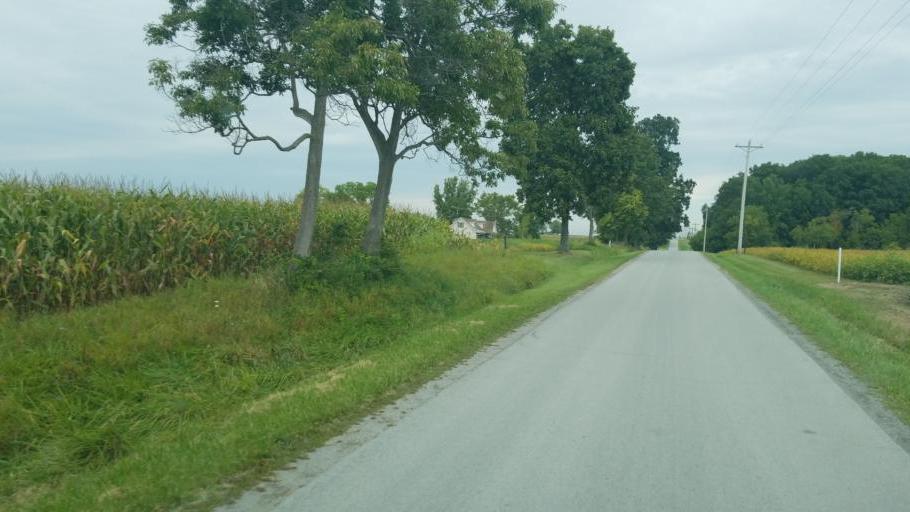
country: US
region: Ohio
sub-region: Wyandot County
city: Upper Sandusky
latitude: 40.7790
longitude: -83.1884
